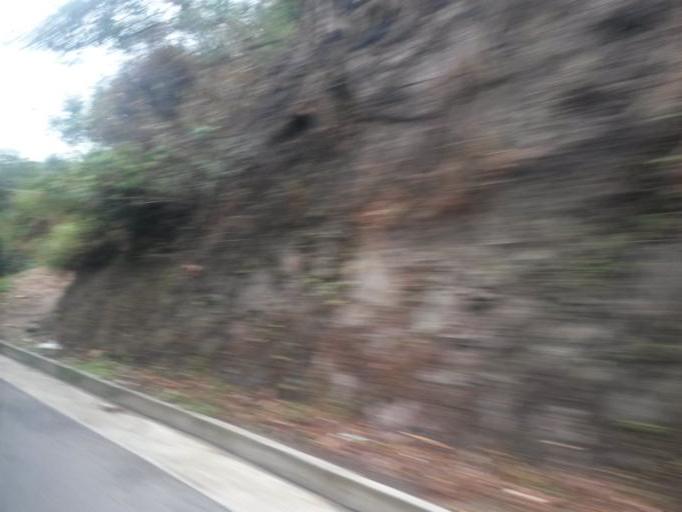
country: CO
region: Cauca
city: Popayan
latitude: 2.4246
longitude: -76.6262
